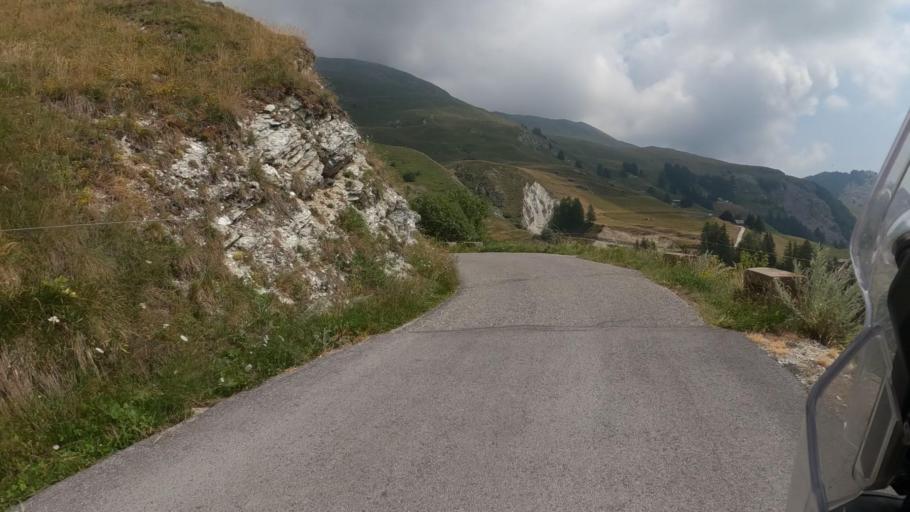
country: IT
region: Piedmont
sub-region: Provincia di Cuneo
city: Campomolino
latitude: 44.3999
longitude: 7.1636
